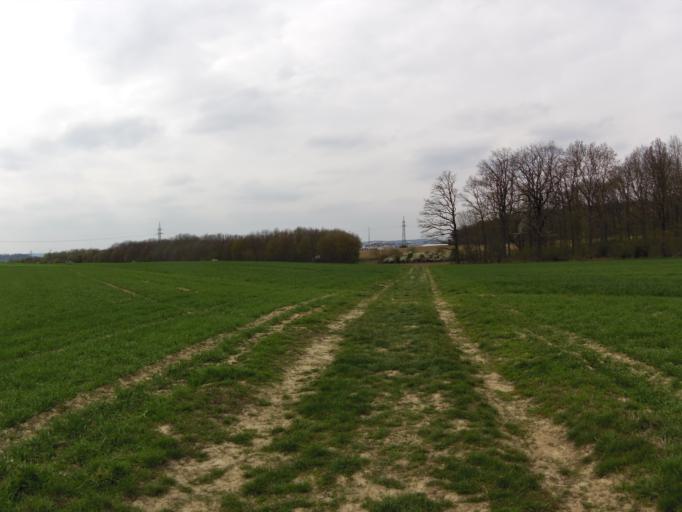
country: DE
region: Bavaria
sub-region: Regierungsbezirk Unterfranken
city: Rottendorf
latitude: 49.7956
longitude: 10.0153
